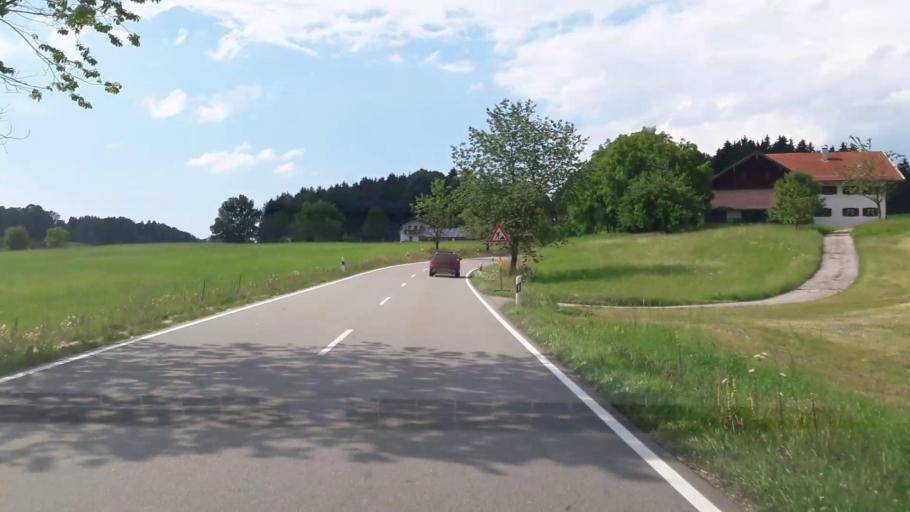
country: DE
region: Bavaria
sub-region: Upper Bavaria
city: Anger
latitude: 47.8057
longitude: 12.8617
